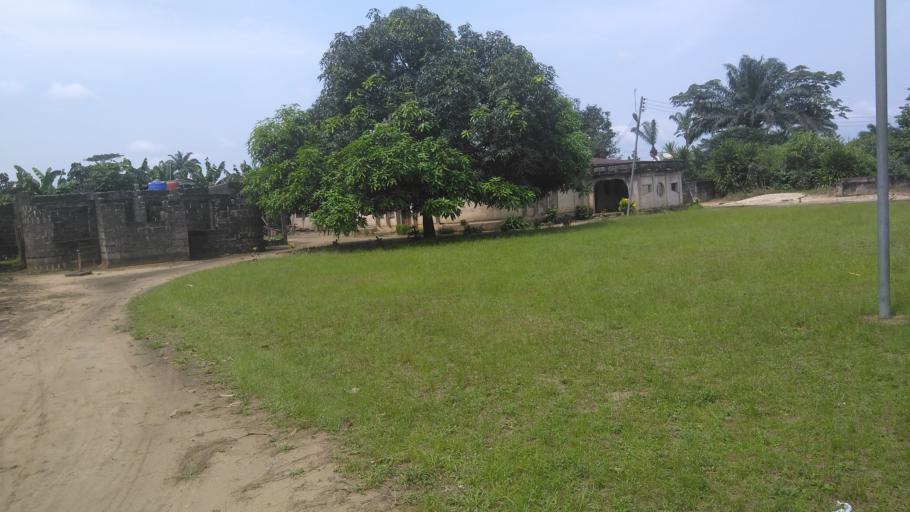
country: NG
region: Abia
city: Aba
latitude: 5.0457
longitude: 7.2498
